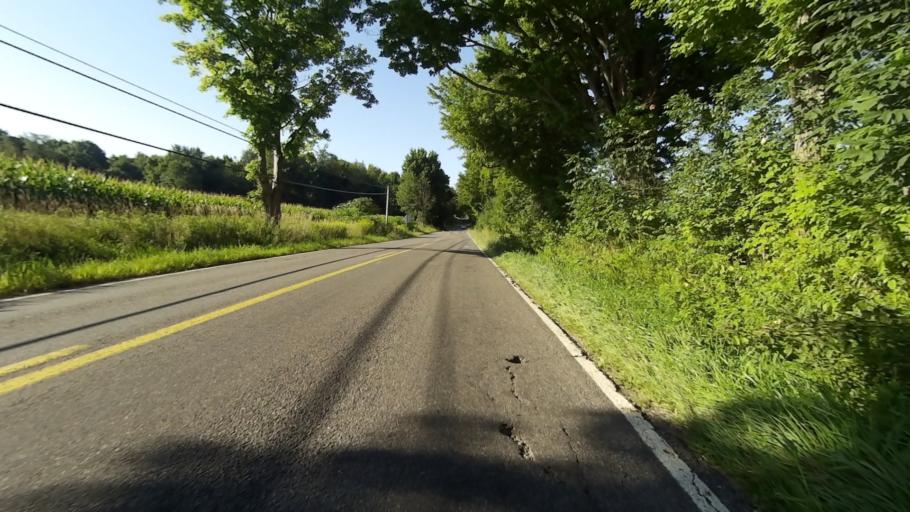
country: US
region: Ohio
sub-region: Portage County
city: Mantua
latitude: 41.2828
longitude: -81.2694
